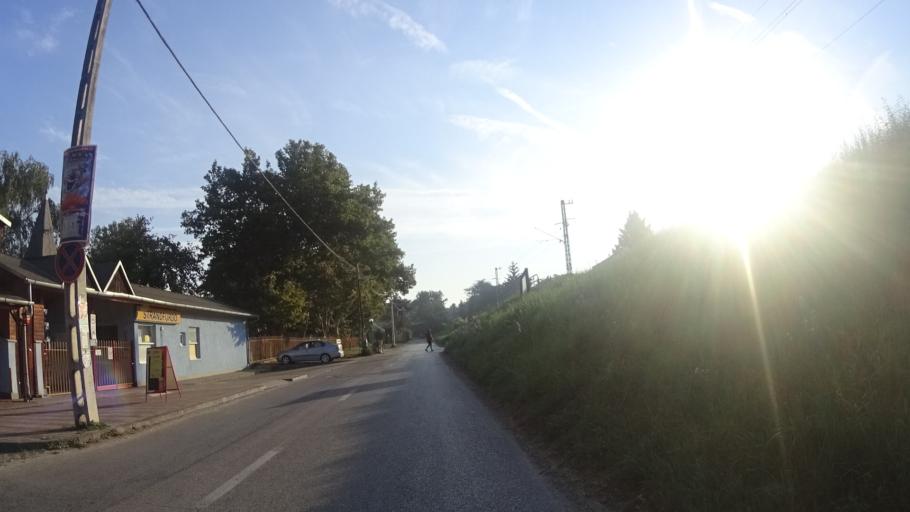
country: HU
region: Somogy
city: Balatonszabadi
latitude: 46.9395
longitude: 18.1285
